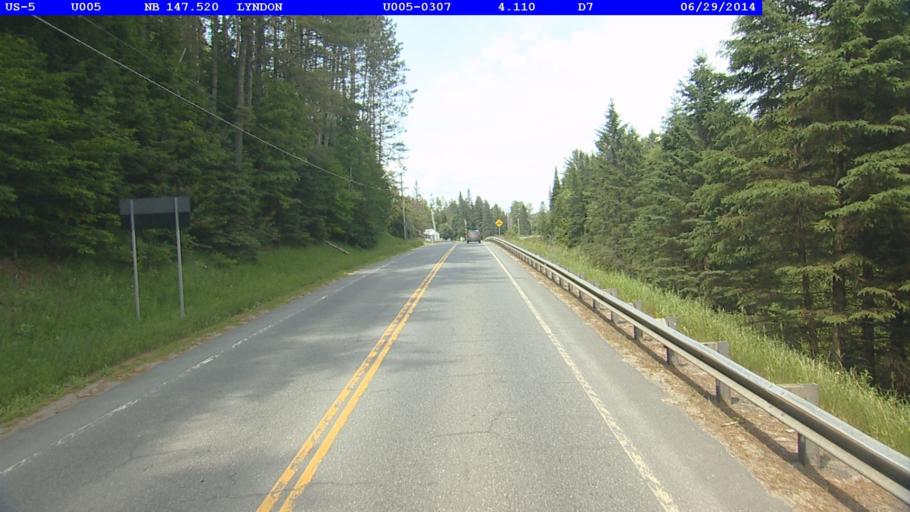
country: US
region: Vermont
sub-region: Caledonia County
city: Lyndonville
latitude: 44.5495
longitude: -72.0026
